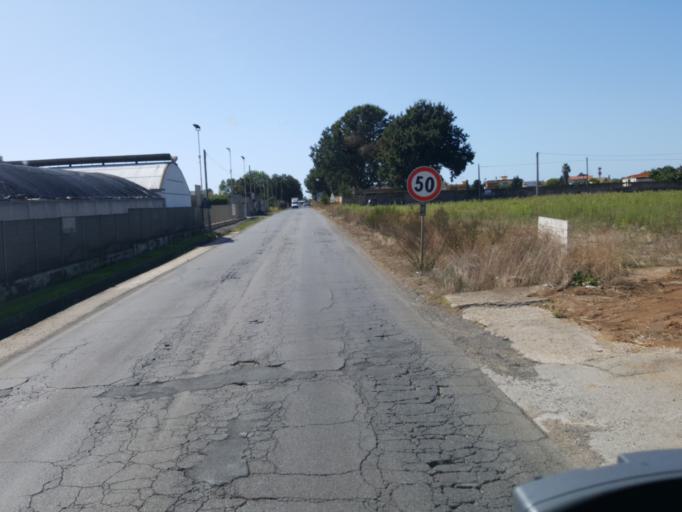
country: IT
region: Latium
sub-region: Citta metropolitana di Roma Capitale
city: Anzio
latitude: 41.5130
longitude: 12.6388
